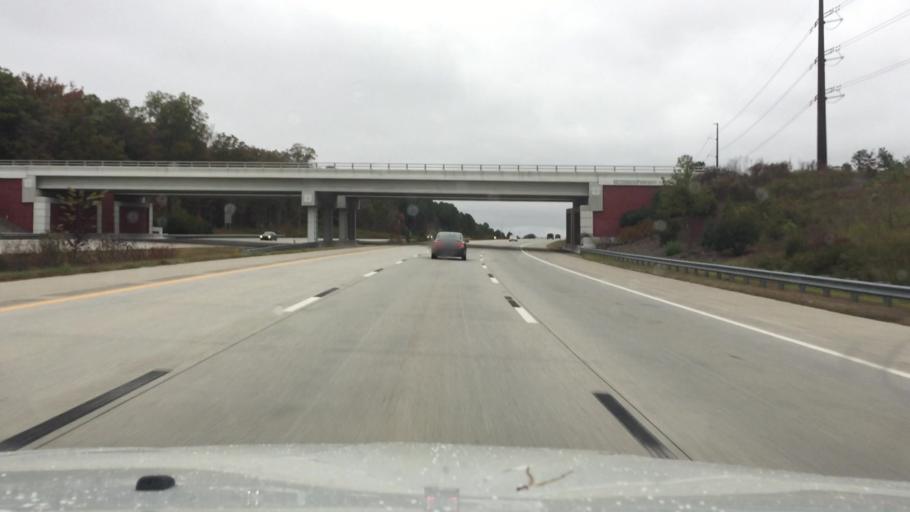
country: US
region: North Carolina
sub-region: Wake County
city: Green Level
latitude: 35.8279
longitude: -78.8934
